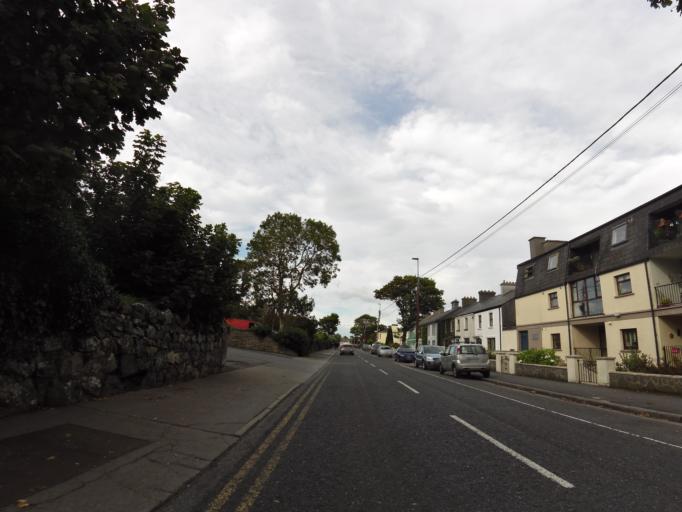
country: IE
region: Connaught
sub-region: County Galway
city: Gaillimh
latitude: 53.2701
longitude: -9.0650
